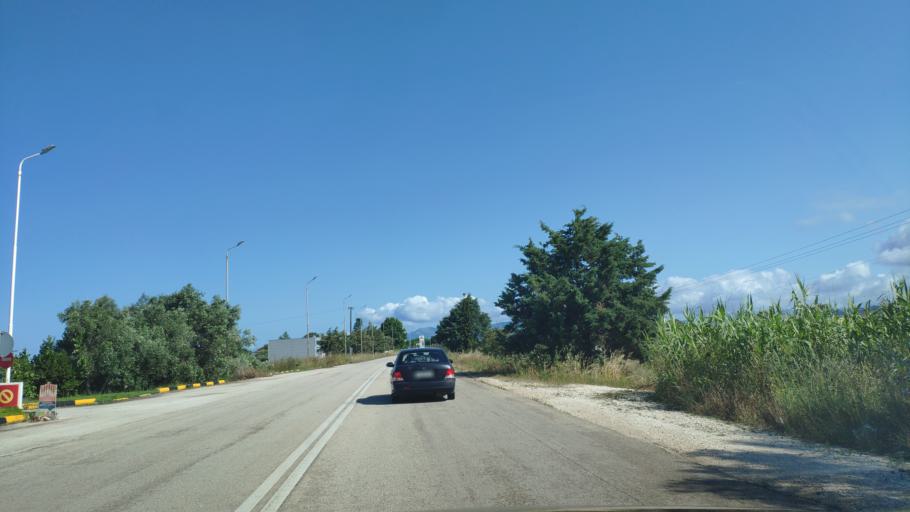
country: GR
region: Epirus
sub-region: Nomos Prevezis
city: Preveza
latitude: 38.9811
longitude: 20.7163
